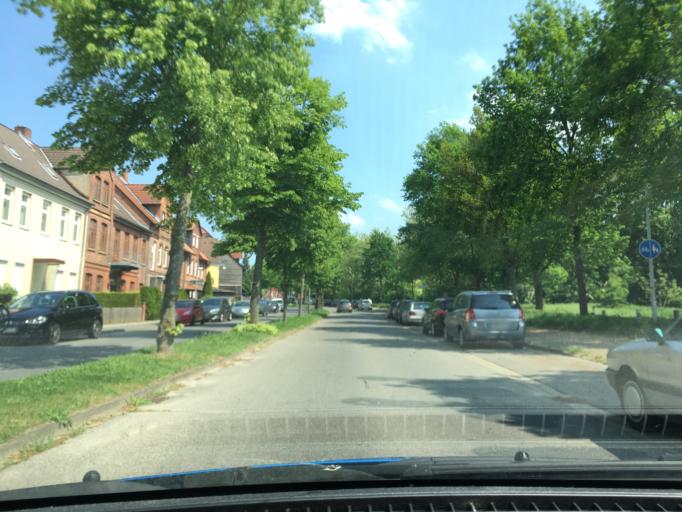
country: DE
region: Lower Saxony
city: Lueneburg
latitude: 53.2476
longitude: 10.3925
